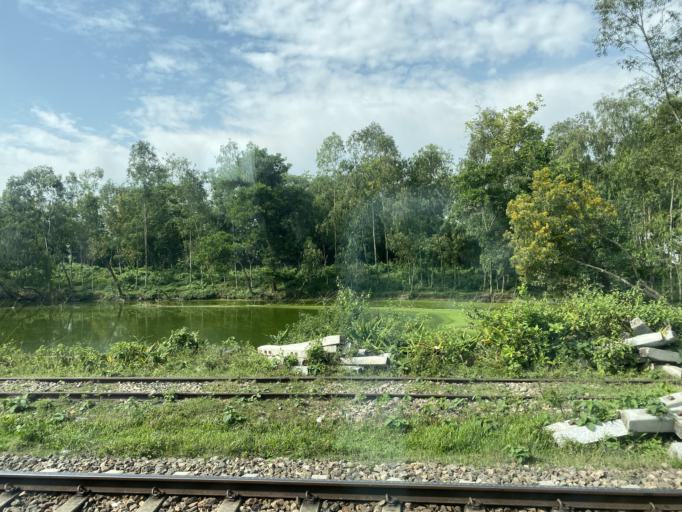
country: BD
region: Sylhet
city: Habiganj
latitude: 24.1777
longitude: 91.3573
